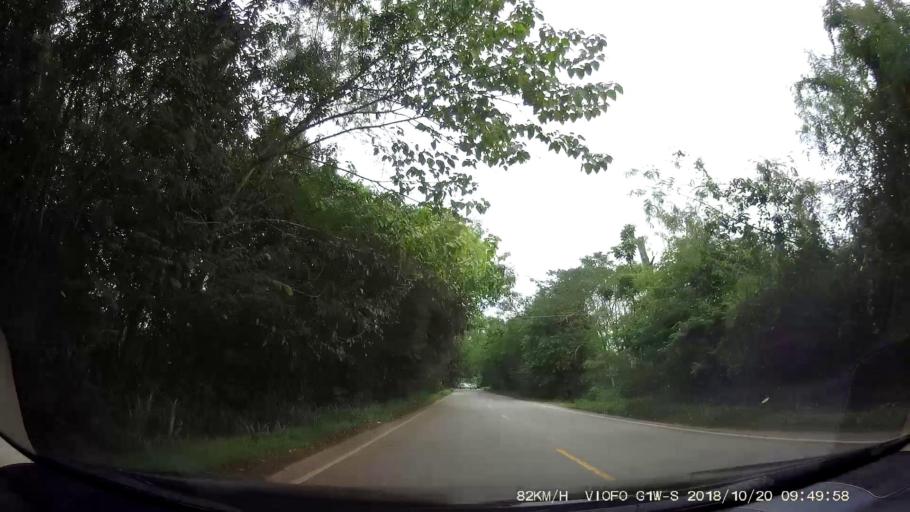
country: TH
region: Chaiyaphum
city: Khon San
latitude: 16.5259
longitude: 101.9035
